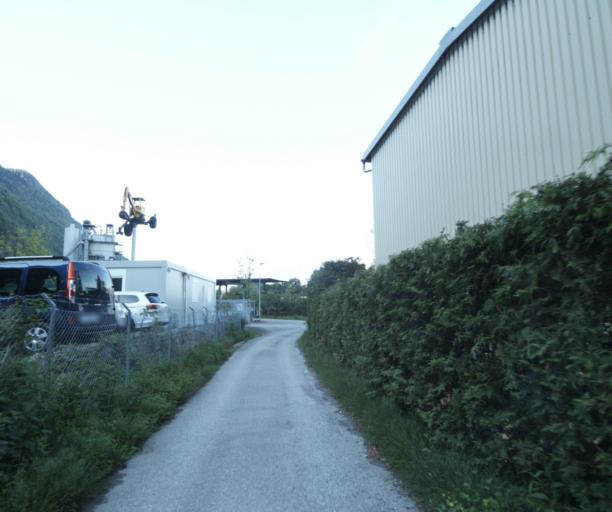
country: CH
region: Vaud
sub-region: Aigle District
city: Villeneuve
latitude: 46.3905
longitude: 6.9389
